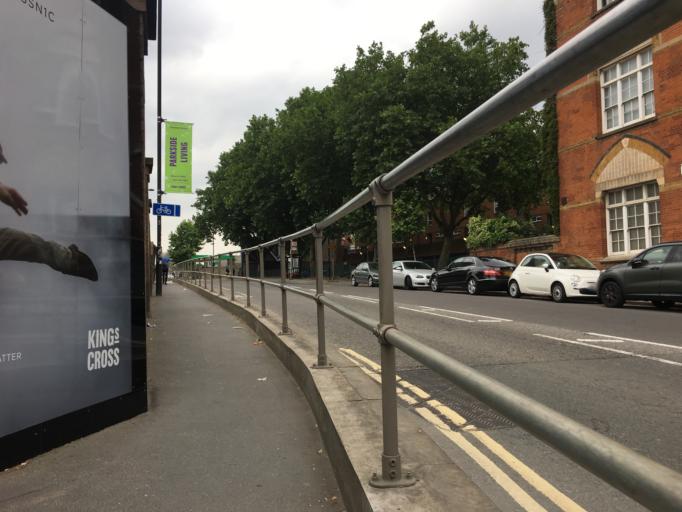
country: GB
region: England
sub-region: Greater London
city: Barnsbury
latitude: 51.5374
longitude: -0.1226
